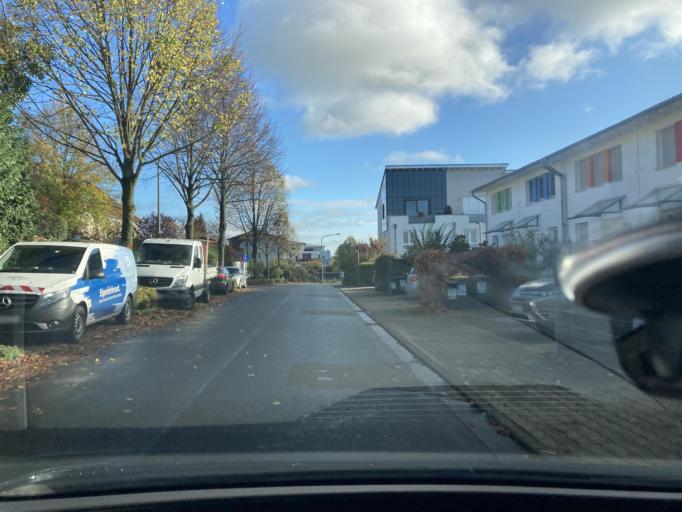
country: DE
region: Hesse
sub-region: Regierungsbezirk Darmstadt
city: Bad Homburg vor der Hoehe
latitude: 50.1748
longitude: 8.6396
